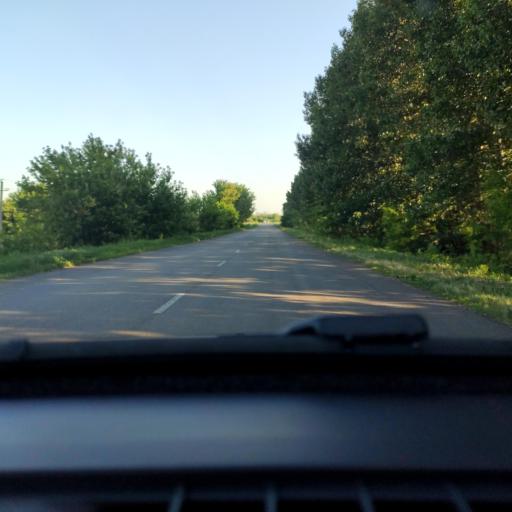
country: RU
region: Voronezj
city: Kashirskoye
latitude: 51.5097
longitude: 39.8325
